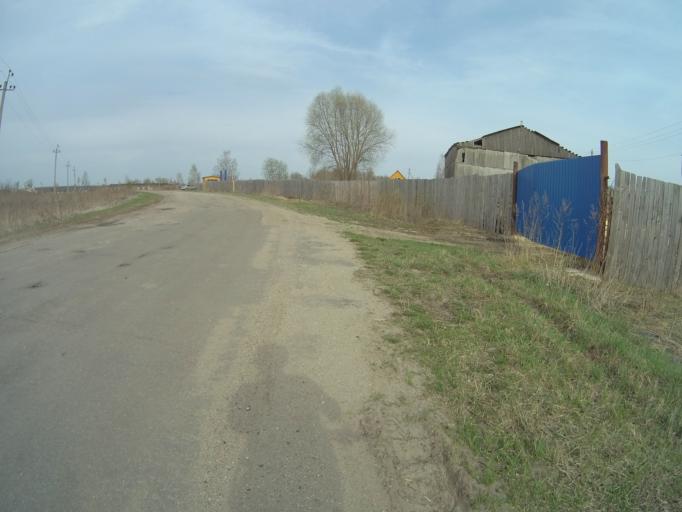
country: RU
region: Vladimir
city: Sudogda
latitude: 55.9717
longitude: 40.7219
